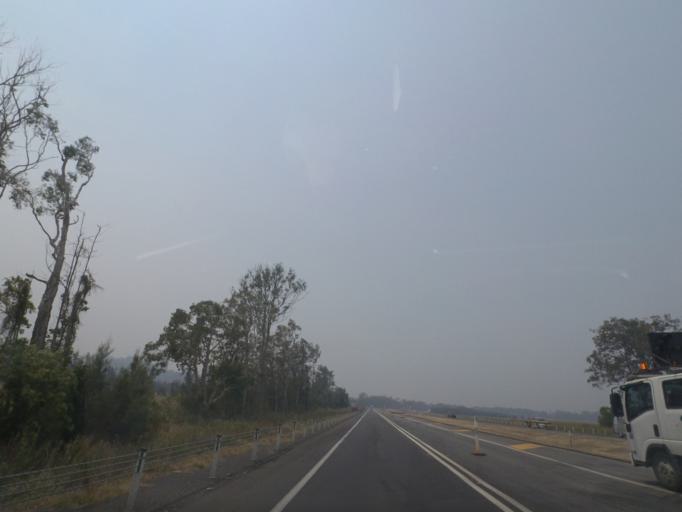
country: AU
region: New South Wales
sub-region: Ballina
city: Ballina
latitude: -28.8736
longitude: 153.4897
